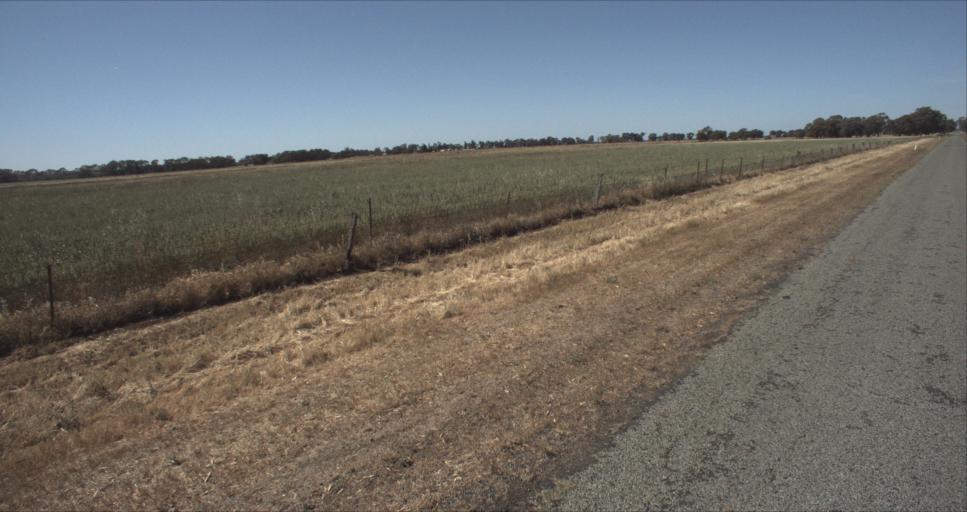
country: AU
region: New South Wales
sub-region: Leeton
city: Leeton
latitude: -34.5352
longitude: 146.3175
